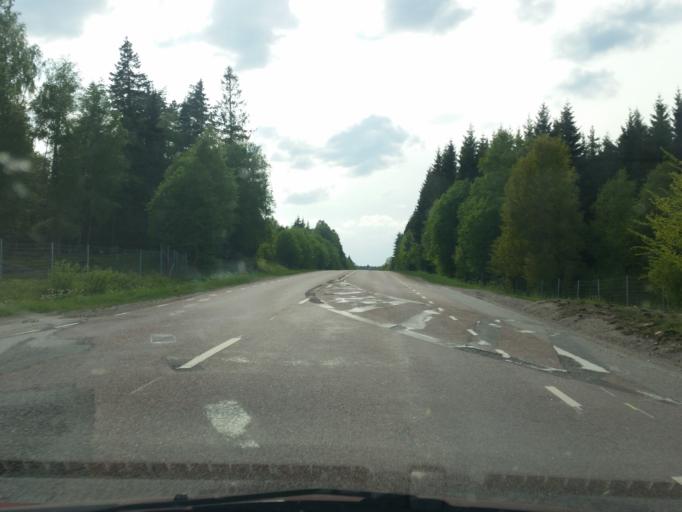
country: SE
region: Vaestra Goetaland
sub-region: Boras Kommun
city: Dalsjofors
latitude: 57.8069
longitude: 13.2130
